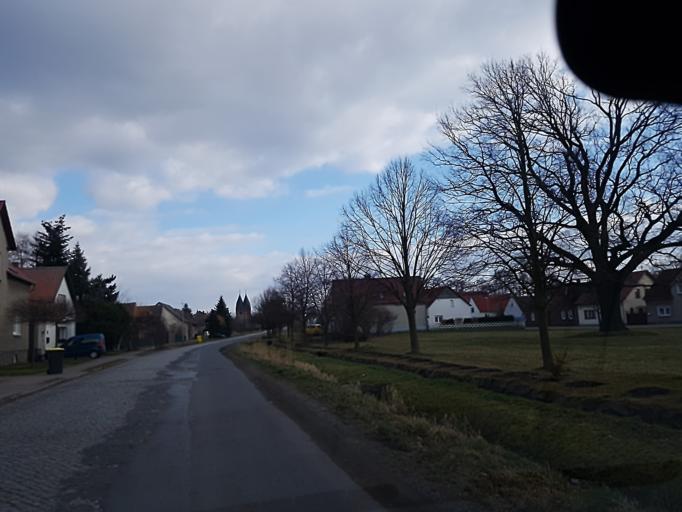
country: DE
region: Brandenburg
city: Doberlug-Kirchhain
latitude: 51.6123
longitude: 13.5905
